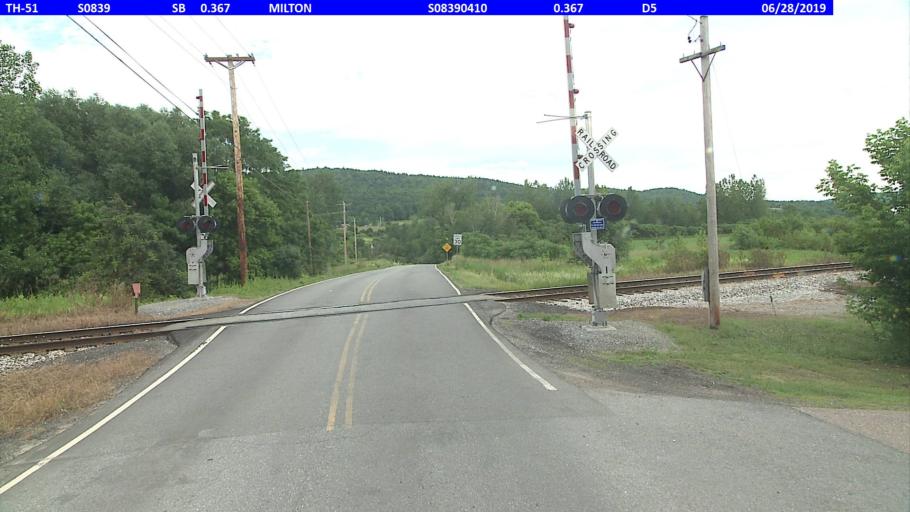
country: US
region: Vermont
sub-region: Chittenden County
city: Milton
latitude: 44.6095
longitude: -73.1094
